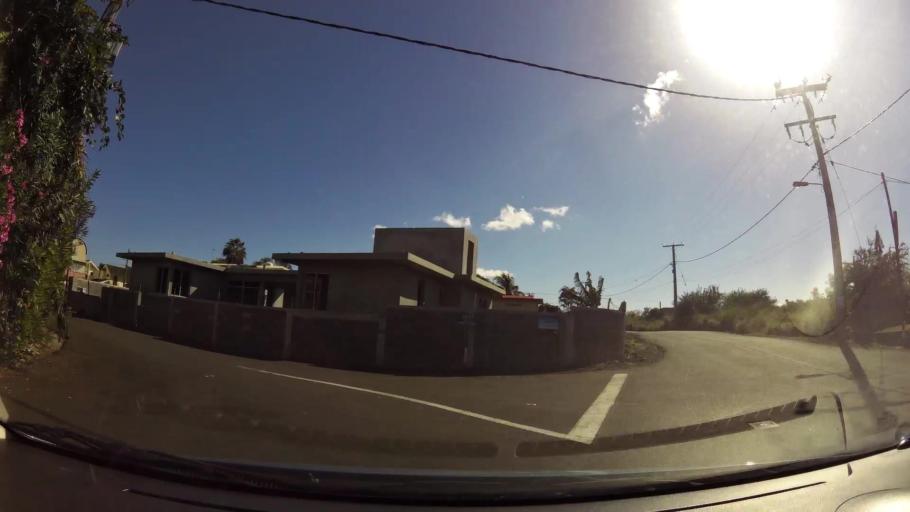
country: MU
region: Black River
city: Flic en Flac
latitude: -20.2758
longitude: 57.3768
